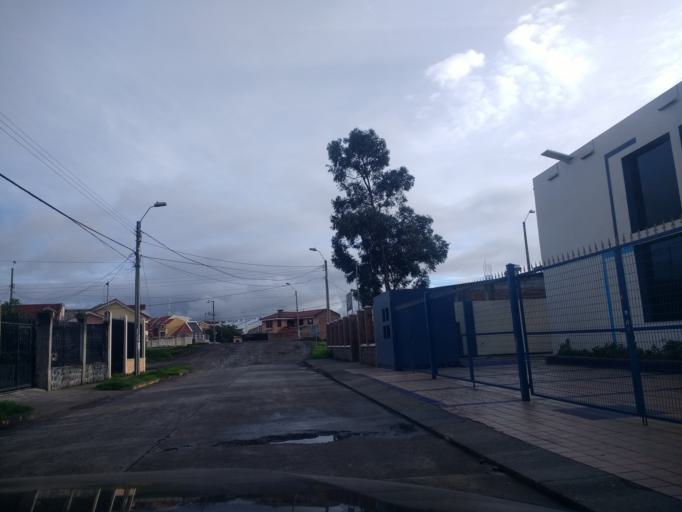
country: EC
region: Azuay
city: Cuenca
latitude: -2.9190
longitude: -79.0444
